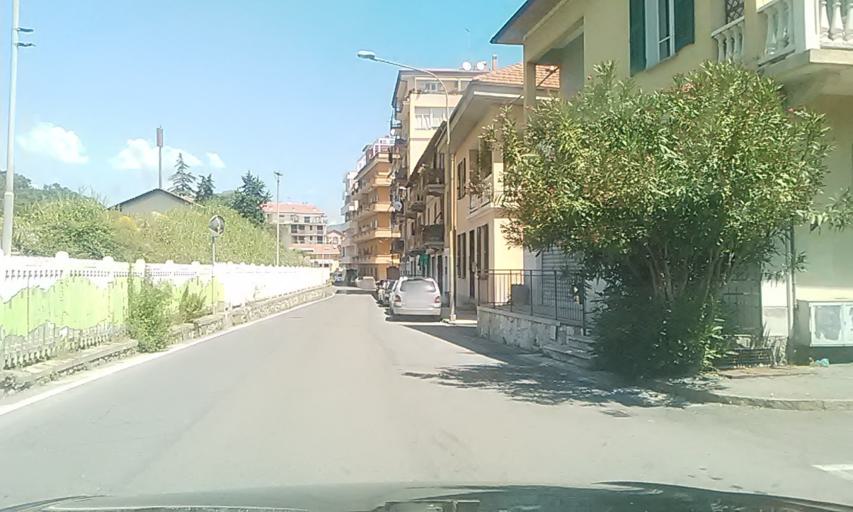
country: IT
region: Liguria
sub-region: Provincia di Savona
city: Andora
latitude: 43.9508
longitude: 8.1398
